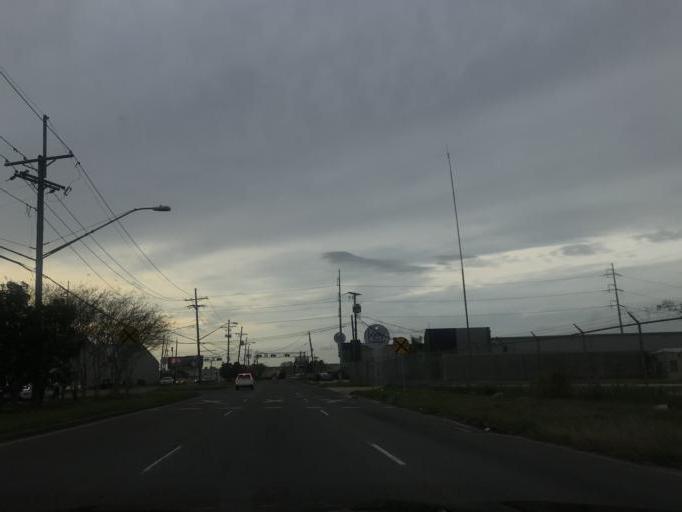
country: US
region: Louisiana
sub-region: Jefferson Parish
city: Jefferson
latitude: 29.9650
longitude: -90.1351
